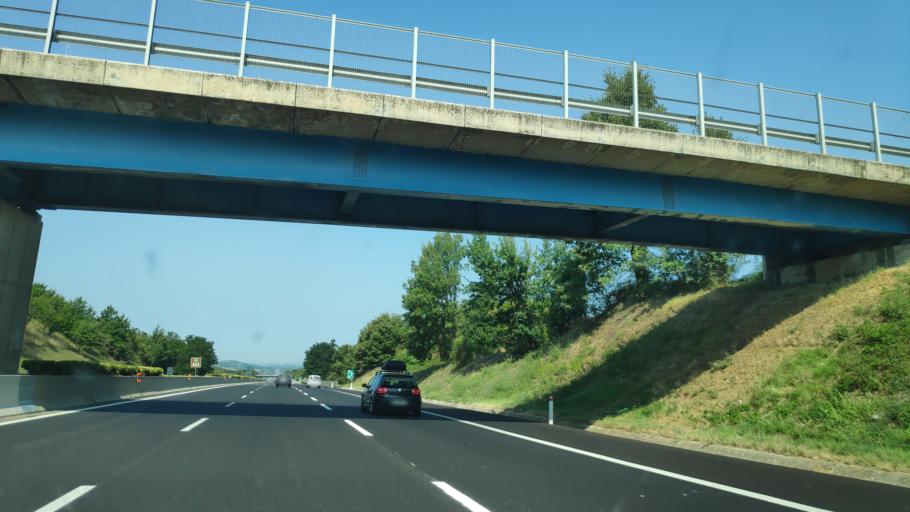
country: IT
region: Campania
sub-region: Provincia di Caserta
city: Mignano Monte Lungo
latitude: 41.4101
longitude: 13.9562
